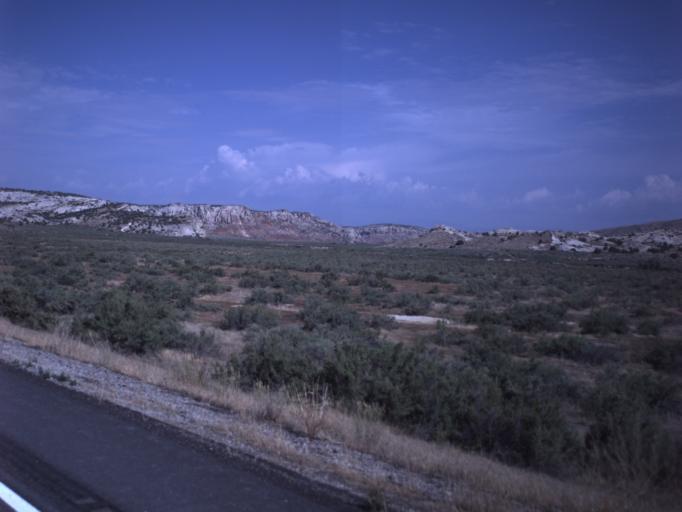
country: US
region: Utah
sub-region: Uintah County
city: Naples
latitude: 40.3164
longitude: -109.2337
